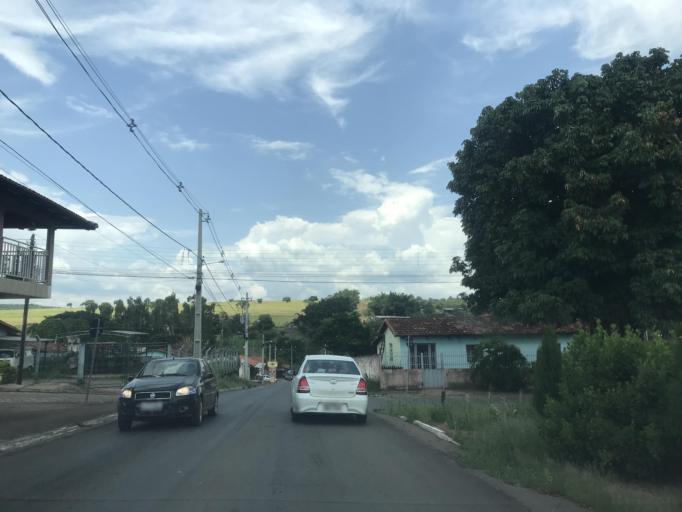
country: BR
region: Goias
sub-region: Bela Vista De Goias
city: Bela Vista de Goias
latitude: -17.0594
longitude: -48.6639
